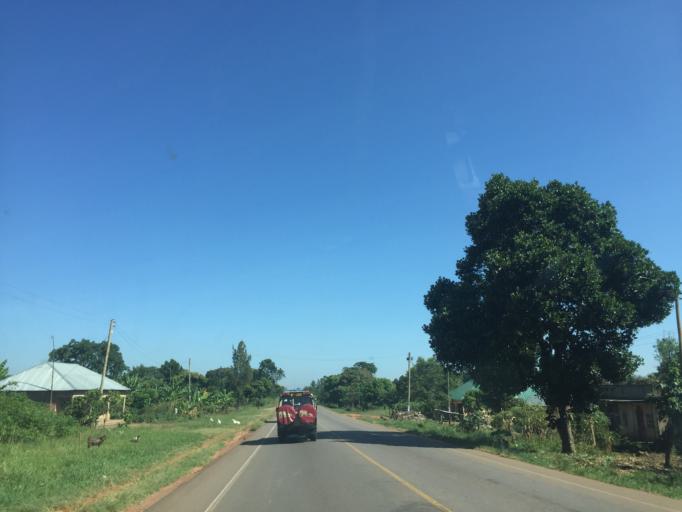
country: UG
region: Central Region
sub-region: Luwero District
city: Wobulenzi
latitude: 0.7690
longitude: 32.5125
